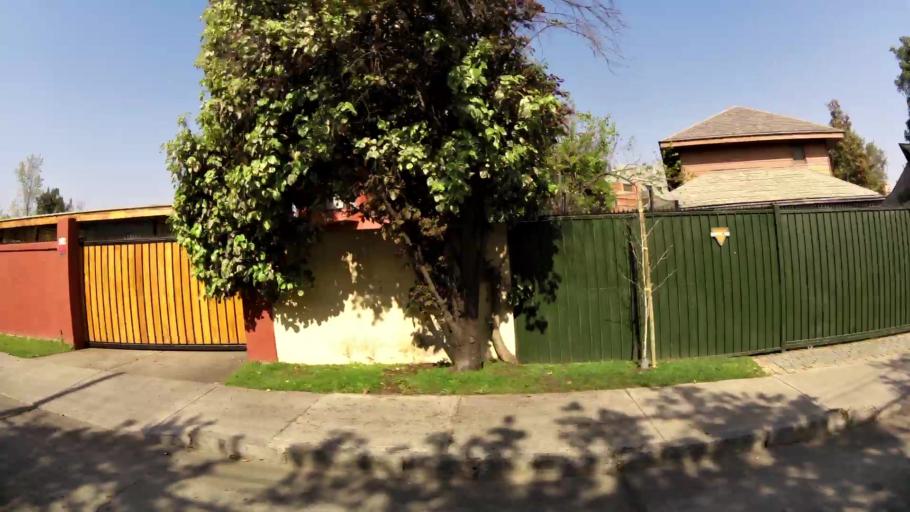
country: CL
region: Santiago Metropolitan
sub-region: Provincia de Santiago
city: Villa Presidente Frei, Nunoa, Santiago, Chile
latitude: -33.3950
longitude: -70.5693
